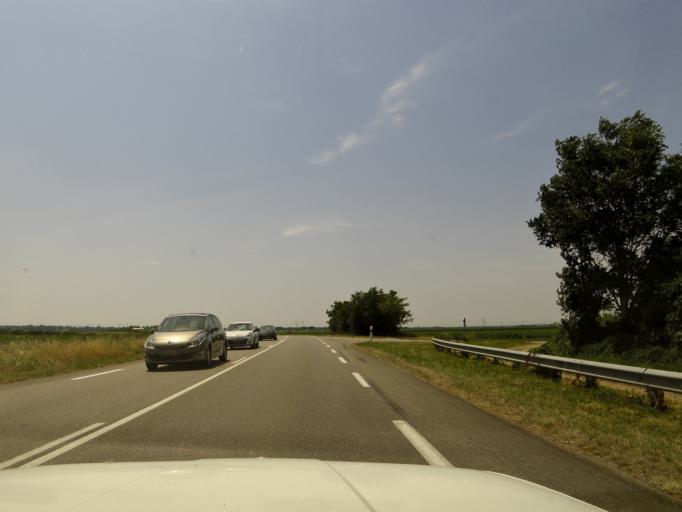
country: FR
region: Rhone-Alpes
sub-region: Departement de l'Ain
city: Perouges
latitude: 45.8775
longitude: 5.1833
